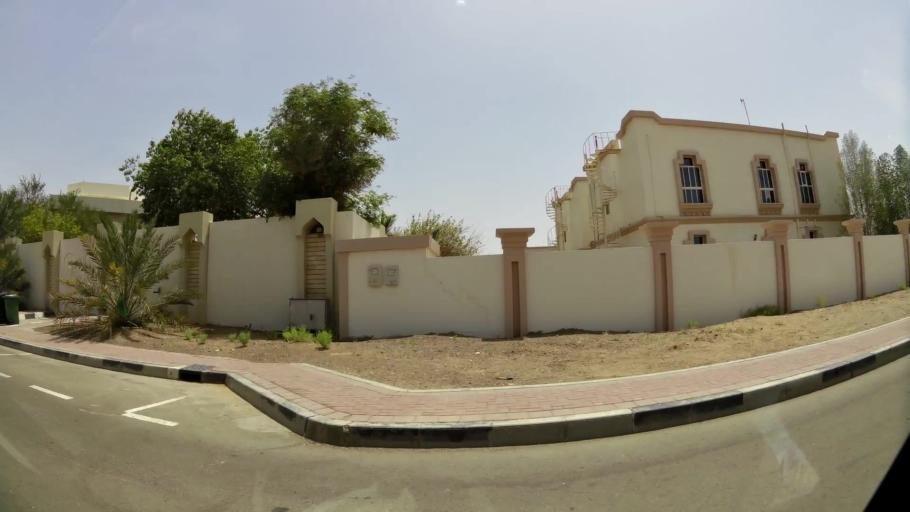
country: AE
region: Abu Dhabi
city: Al Ain
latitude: 24.1849
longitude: 55.7259
